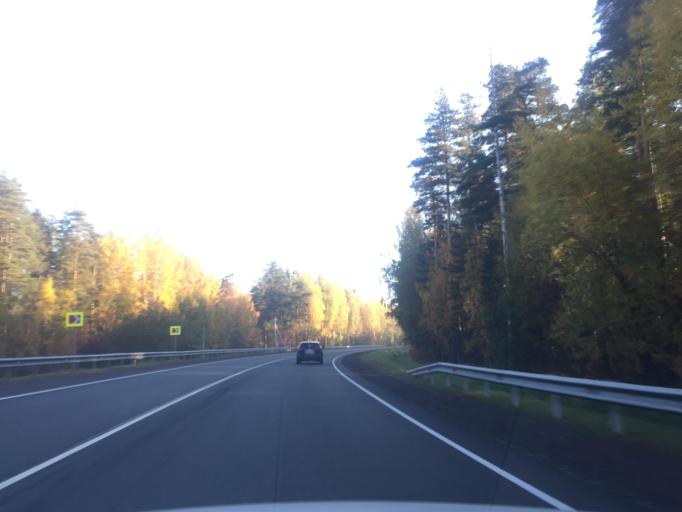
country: RU
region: Leningrad
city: Sapernoye
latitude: 60.7320
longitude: 30.0756
